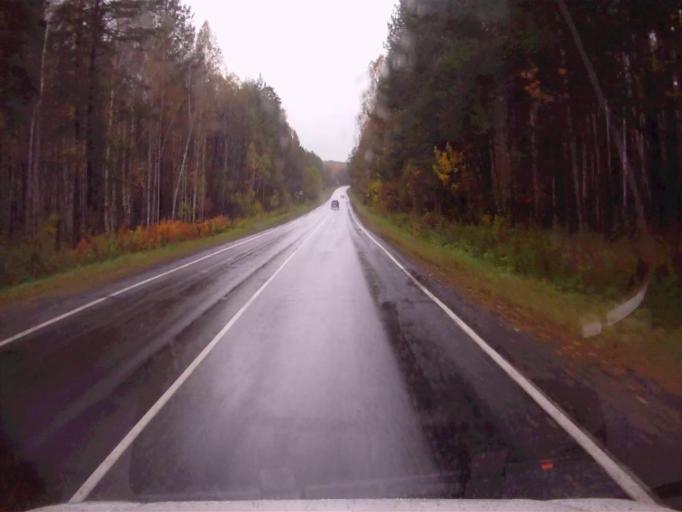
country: RU
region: Chelyabinsk
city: Verkhniy Ufaley
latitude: 55.9696
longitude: 60.3660
